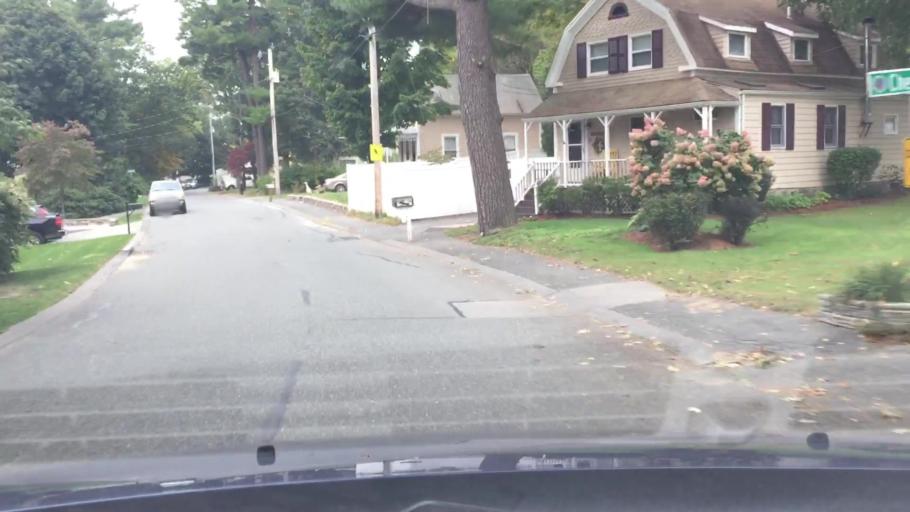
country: US
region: Massachusetts
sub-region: Essex County
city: Middleton
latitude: 42.5808
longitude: -71.0052
